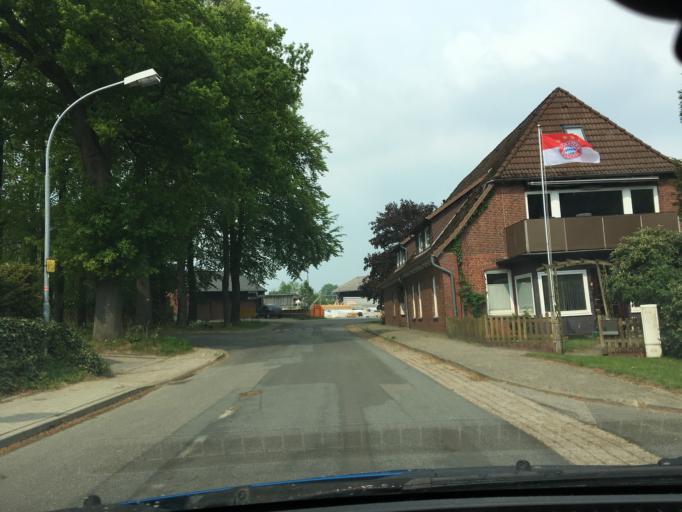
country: DE
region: Lower Saxony
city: Seevetal
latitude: 53.4211
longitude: 9.8933
